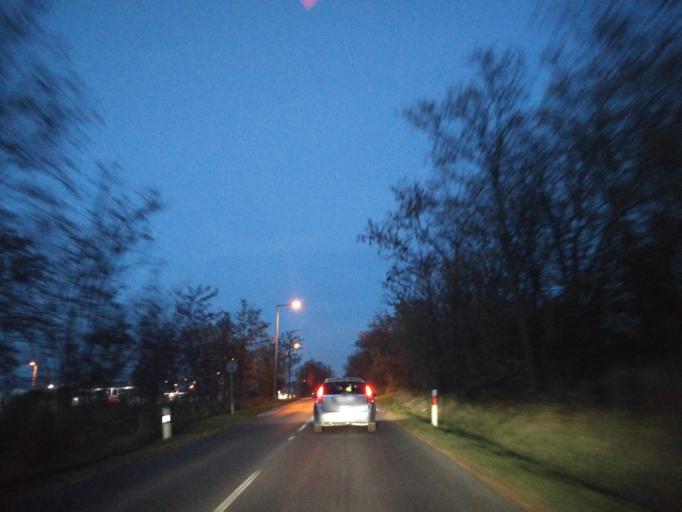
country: HU
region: Pest
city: Budakeszi
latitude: 47.4964
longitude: 18.9151
